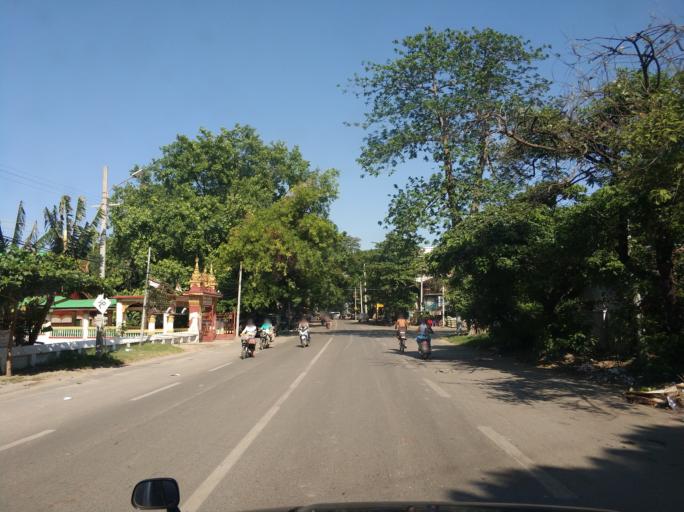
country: MM
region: Mandalay
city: Mandalay
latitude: 21.9713
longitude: 96.0586
